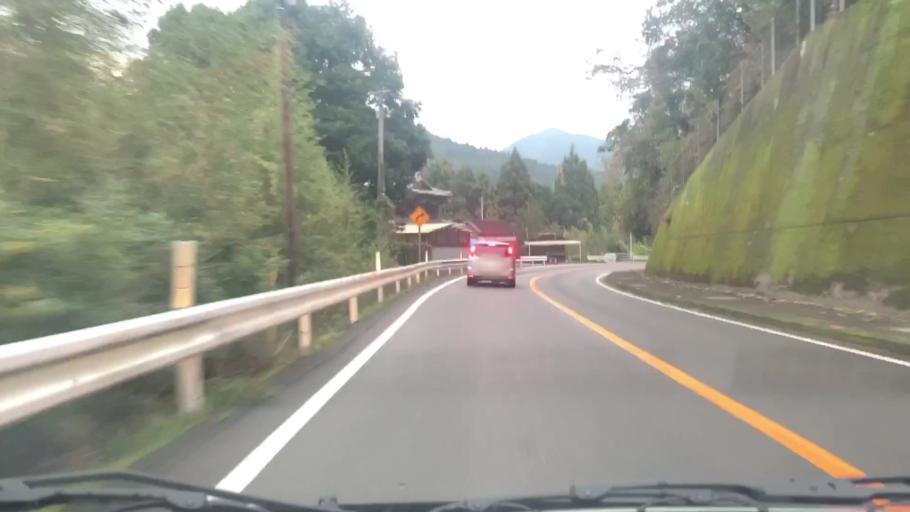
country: JP
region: Saga Prefecture
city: Ureshinomachi-shimojuku
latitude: 33.0587
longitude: 129.9489
